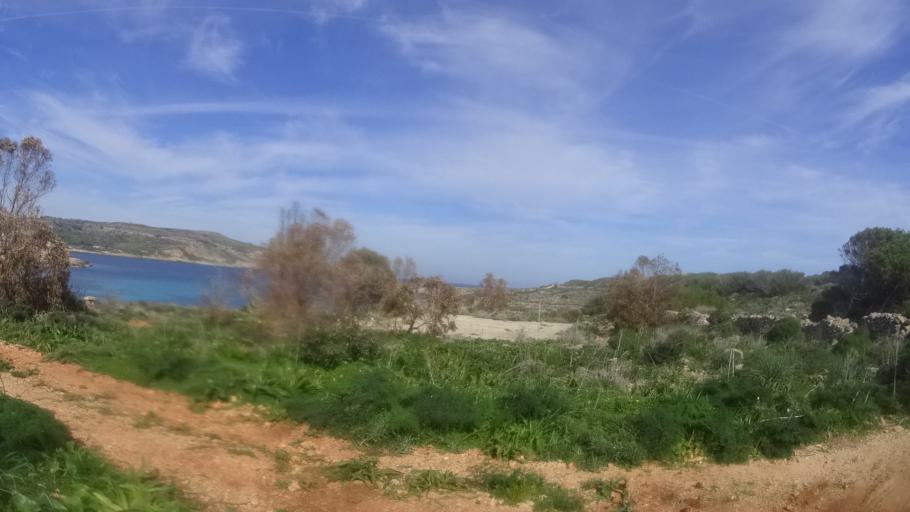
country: MT
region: Il-Qala
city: Qala
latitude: 36.0159
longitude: 14.3299
